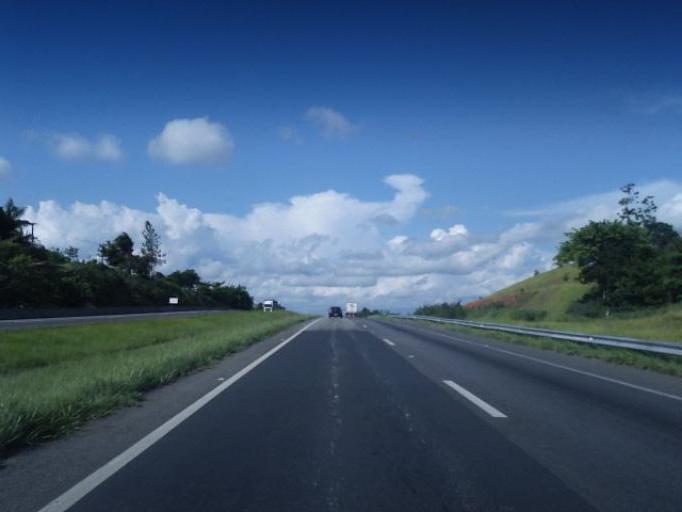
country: BR
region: Sao Paulo
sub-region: Registro
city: Registro
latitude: -24.4678
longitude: -47.8215
